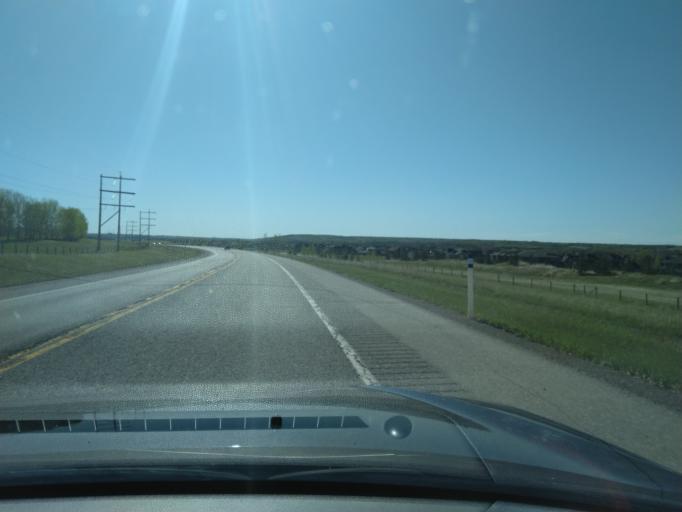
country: CA
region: Alberta
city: Cochrane
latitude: 51.0201
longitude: -114.3234
